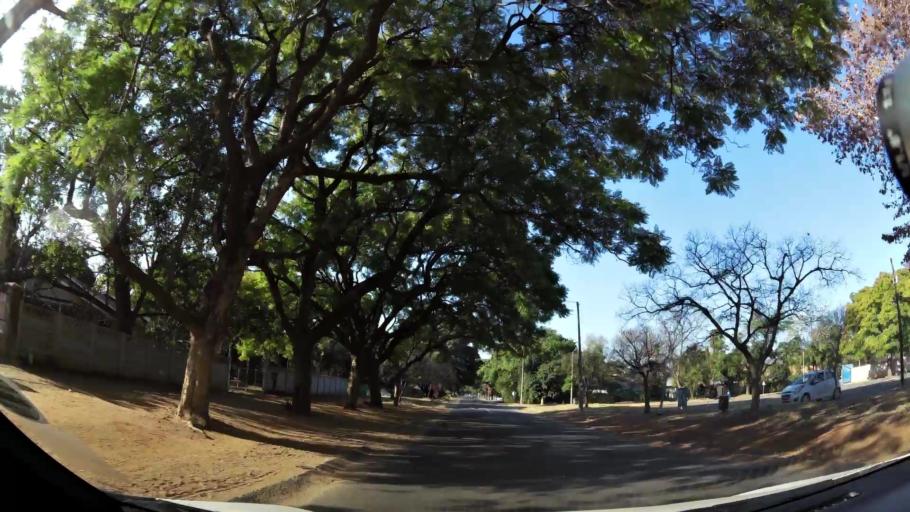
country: ZA
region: North-West
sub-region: Bojanala Platinum District Municipality
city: Rustenburg
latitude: -25.6739
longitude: 27.2334
